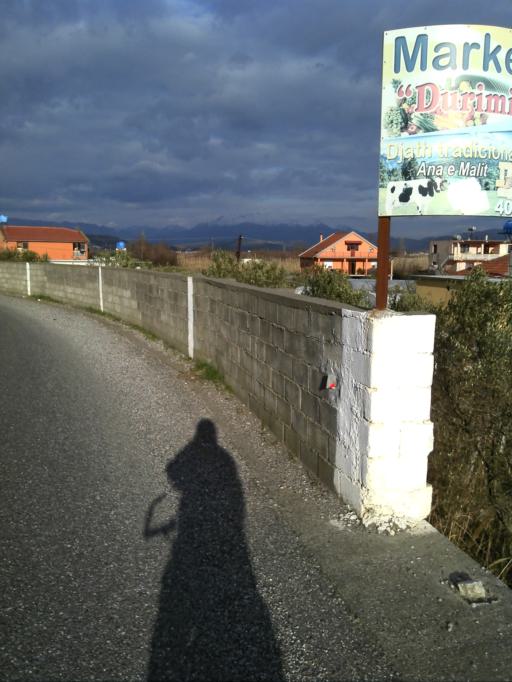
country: AL
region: Shkoder
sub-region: Rrethi i Shkodres
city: Berdica e Madhe
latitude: 42.0253
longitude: 19.4686
